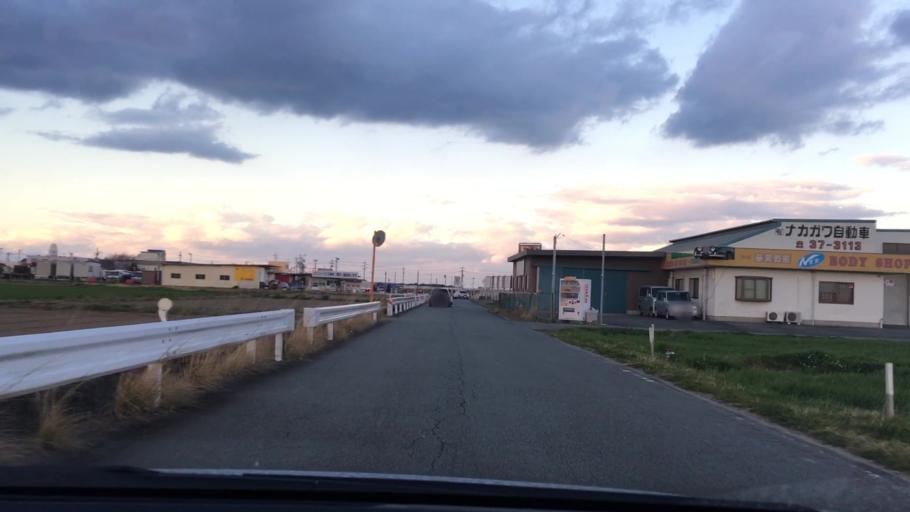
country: JP
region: Mie
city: Ise
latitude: 34.5309
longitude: 136.6772
